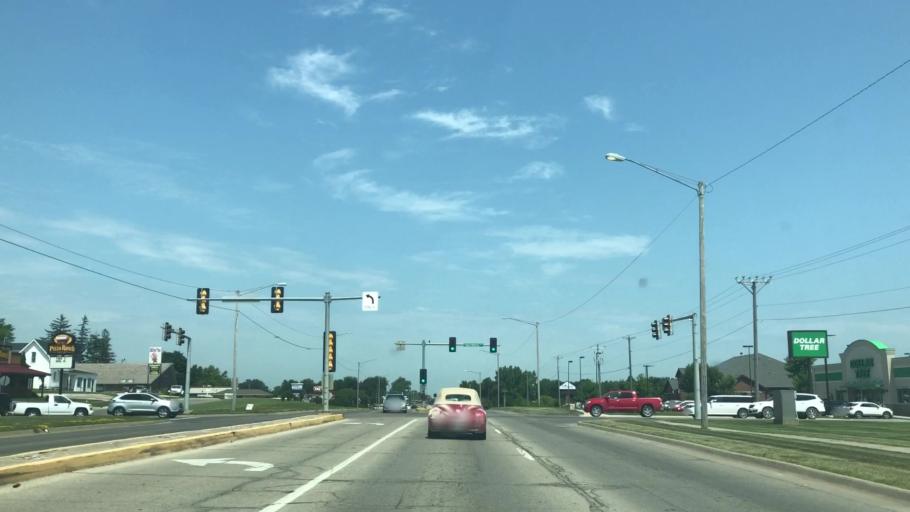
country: US
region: Iowa
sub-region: Marshall County
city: Marshalltown
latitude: 42.0174
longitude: -92.9122
